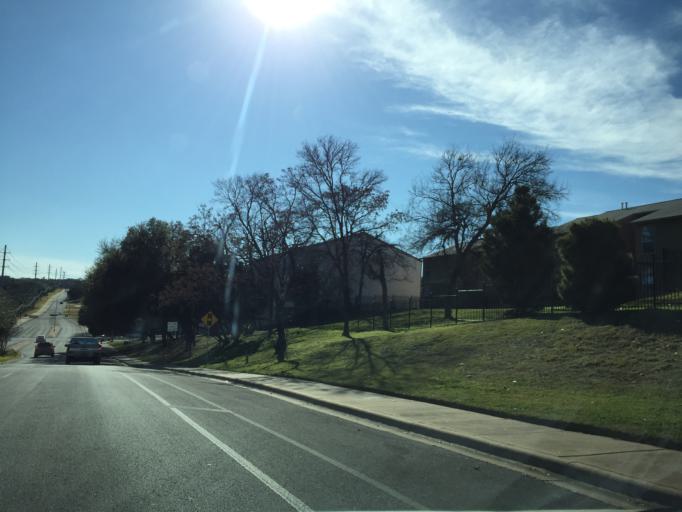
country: US
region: Texas
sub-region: Travis County
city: Austin
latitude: 30.2289
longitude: -97.7270
